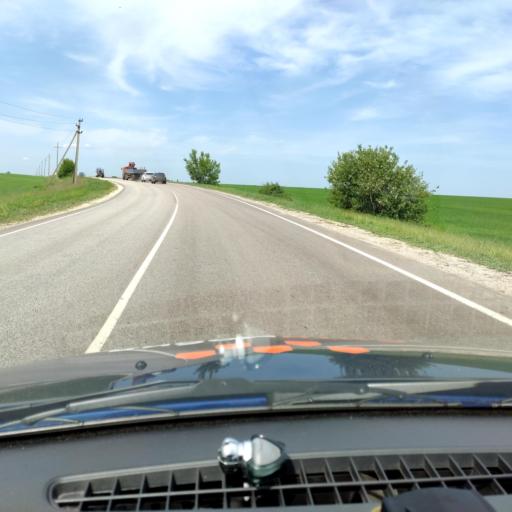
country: RU
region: Voronezj
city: Novaya Usman'
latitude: 51.5563
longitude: 39.3760
